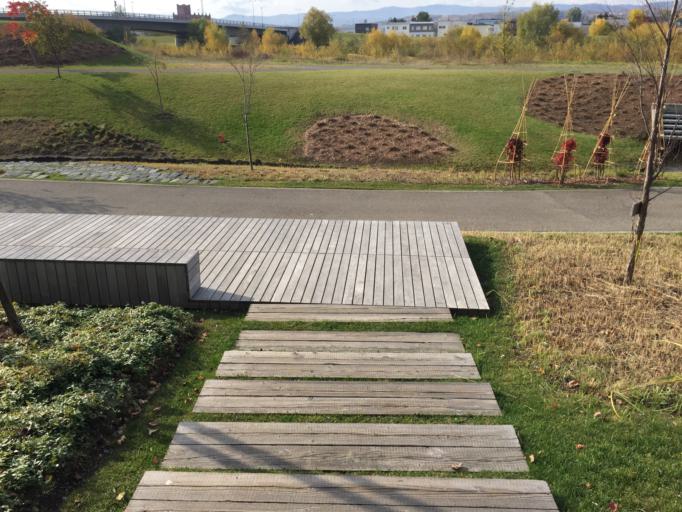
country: JP
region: Hokkaido
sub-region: Asahikawa-shi
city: Asahikawa
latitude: 43.7621
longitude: 142.3585
